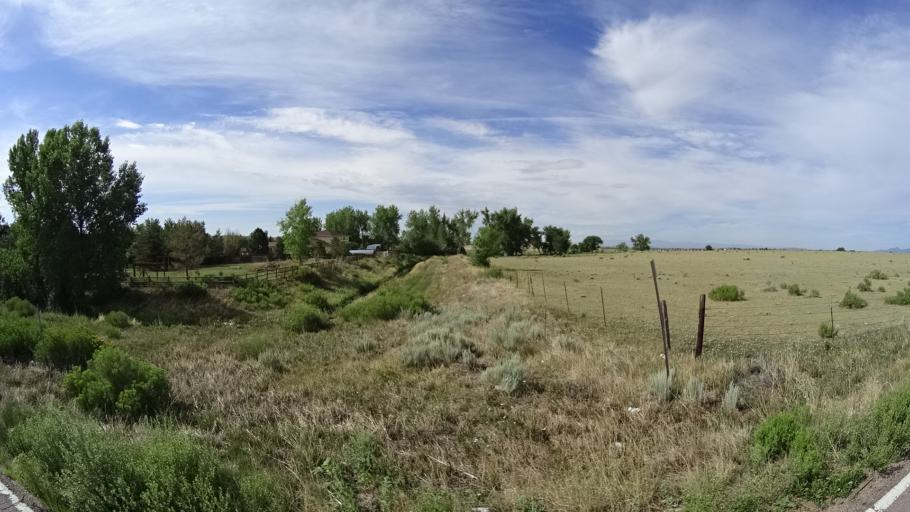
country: US
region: Colorado
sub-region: El Paso County
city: Security-Widefield
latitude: 38.7375
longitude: -104.6551
